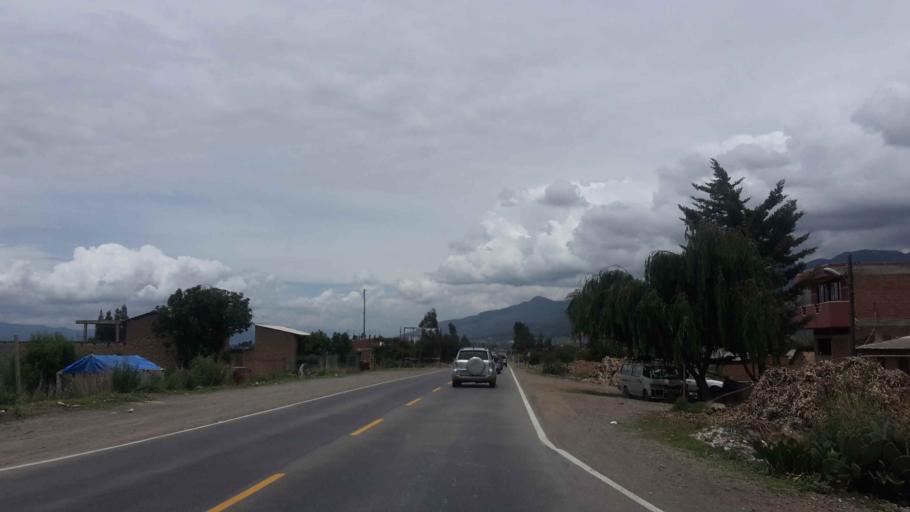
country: BO
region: Cochabamba
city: Punata
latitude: -17.5148
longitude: -65.8273
